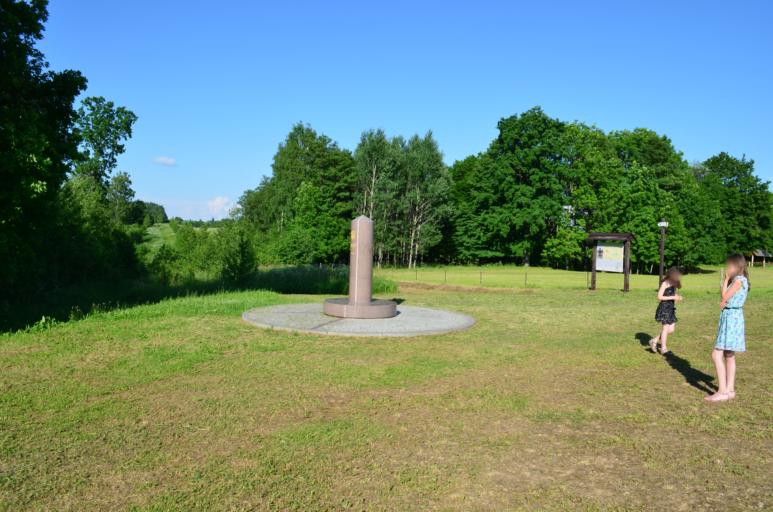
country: PL
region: Podlasie
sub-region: Powiat suwalski
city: Filipow
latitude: 54.3632
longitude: 22.7919
